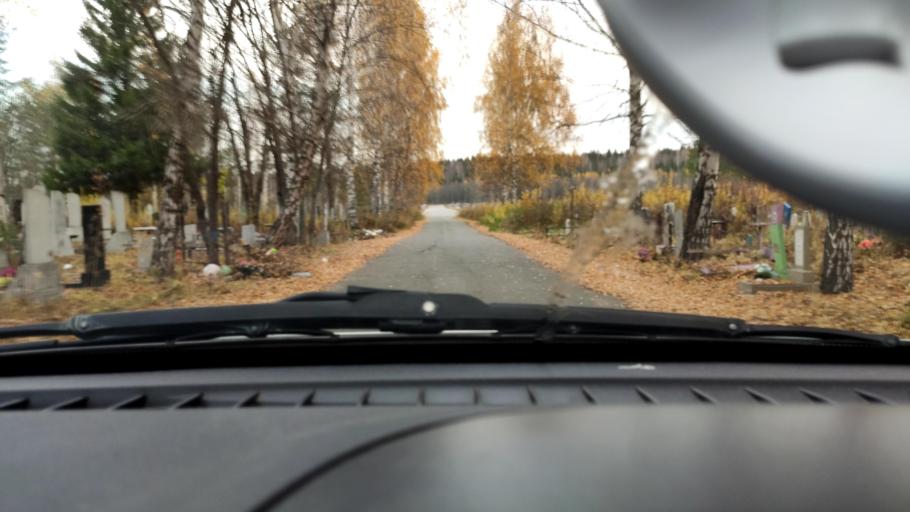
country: RU
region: Perm
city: Kondratovo
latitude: 58.0680
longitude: 56.1355
